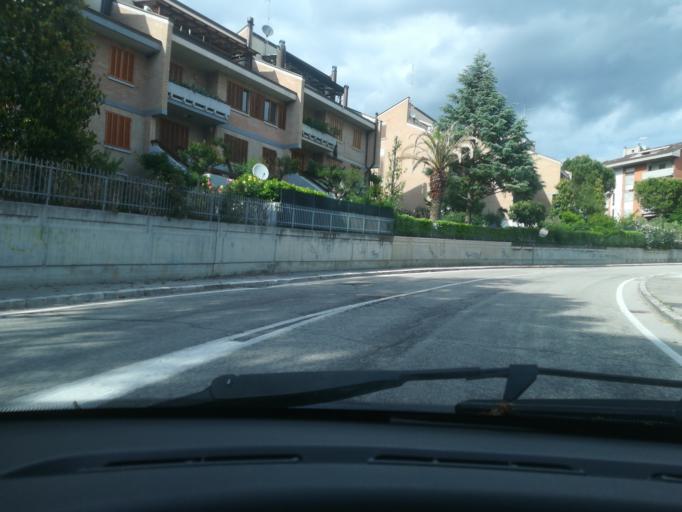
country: IT
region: The Marches
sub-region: Provincia di Macerata
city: Macerata
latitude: 43.2898
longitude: 13.4304
